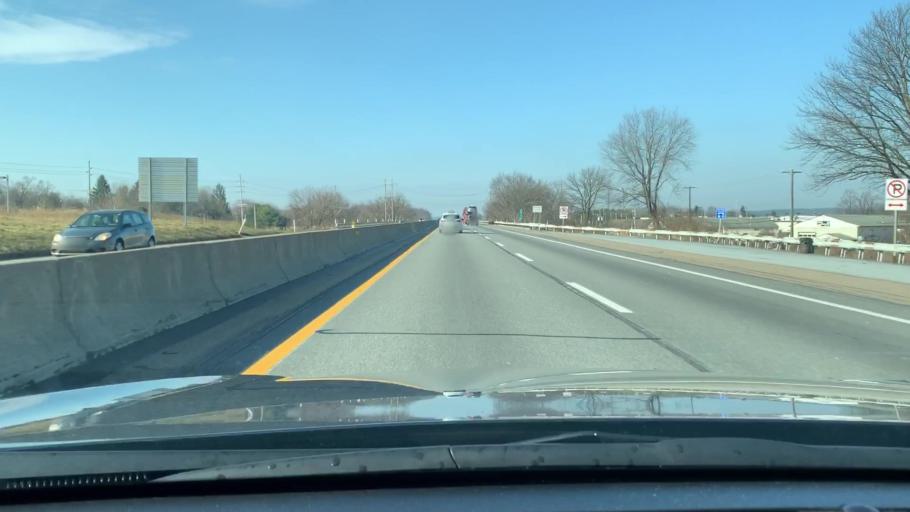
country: US
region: Pennsylvania
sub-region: Chester County
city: Chester Springs
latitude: 40.0702
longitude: -75.6767
